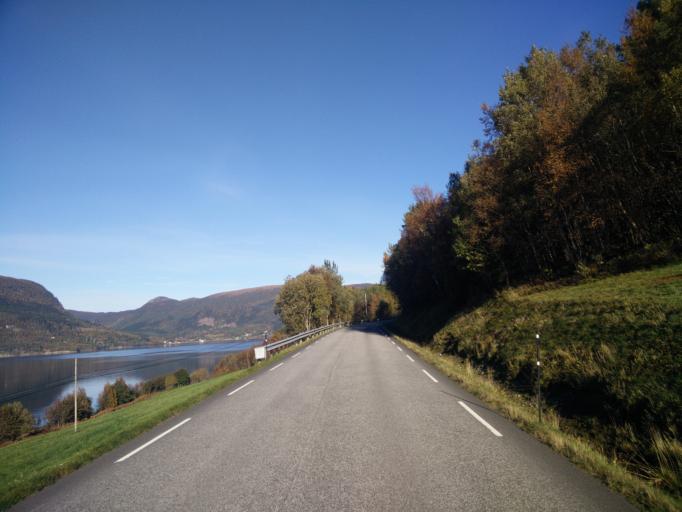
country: NO
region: More og Romsdal
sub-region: Halsa
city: Liaboen
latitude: 63.1361
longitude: 8.4107
